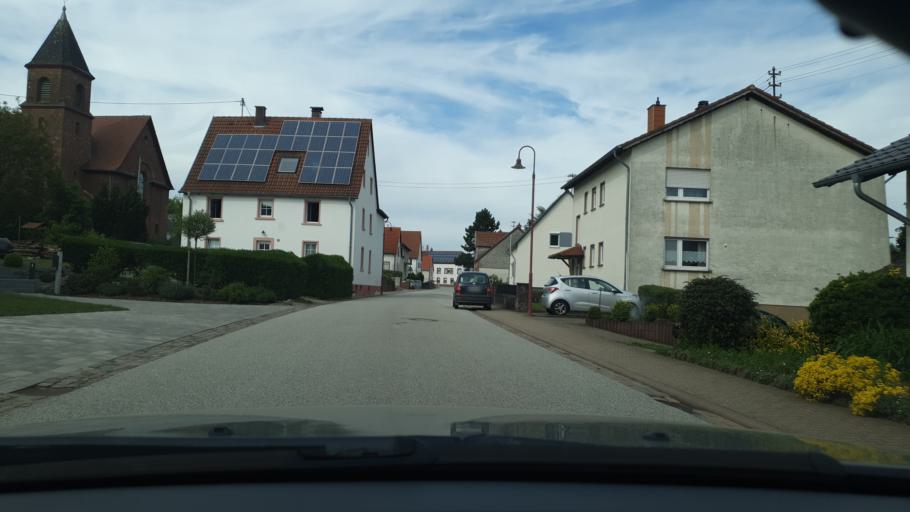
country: DE
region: Rheinland-Pfalz
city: Mittelbrunn
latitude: 49.3721
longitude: 7.5499
